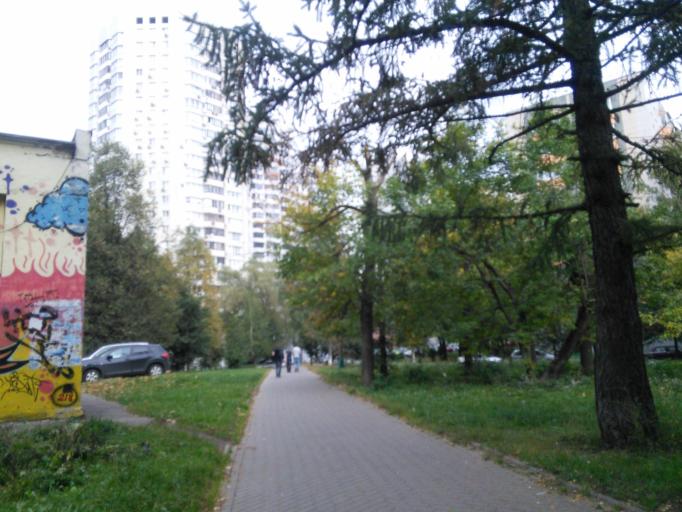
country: RU
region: Moskovskaya
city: Levoberezhnyy
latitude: 55.8612
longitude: 37.4739
